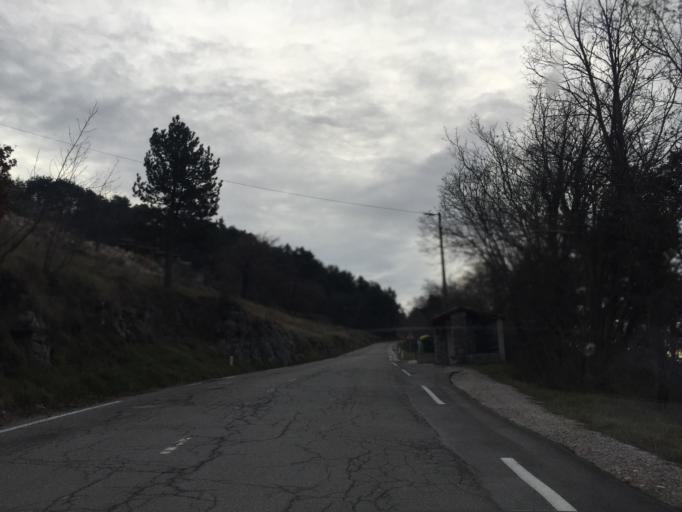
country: SI
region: Nova Gorica
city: Kromberk
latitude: 45.9838
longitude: 13.7118
